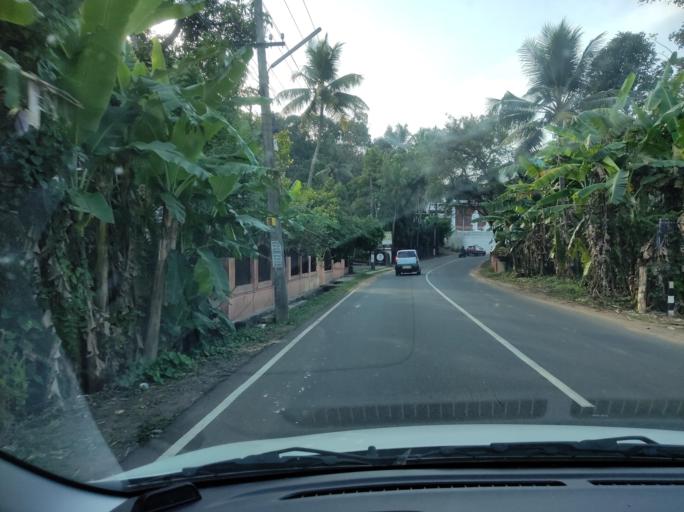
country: IN
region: Kerala
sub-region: Kottayam
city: Kottayam
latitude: 9.6464
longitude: 76.5247
